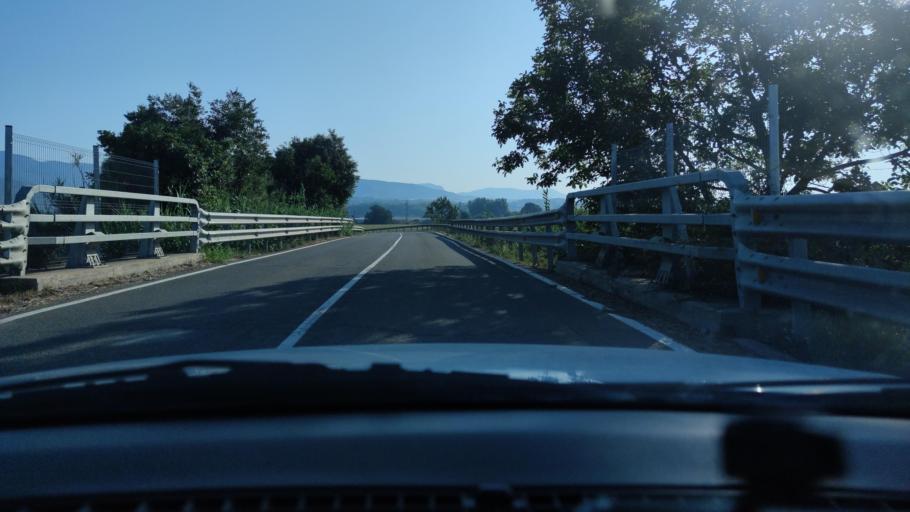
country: ES
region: Catalonia
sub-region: Provincia de Lleida
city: Balaguer
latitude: 41.8311
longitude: 0.8131
